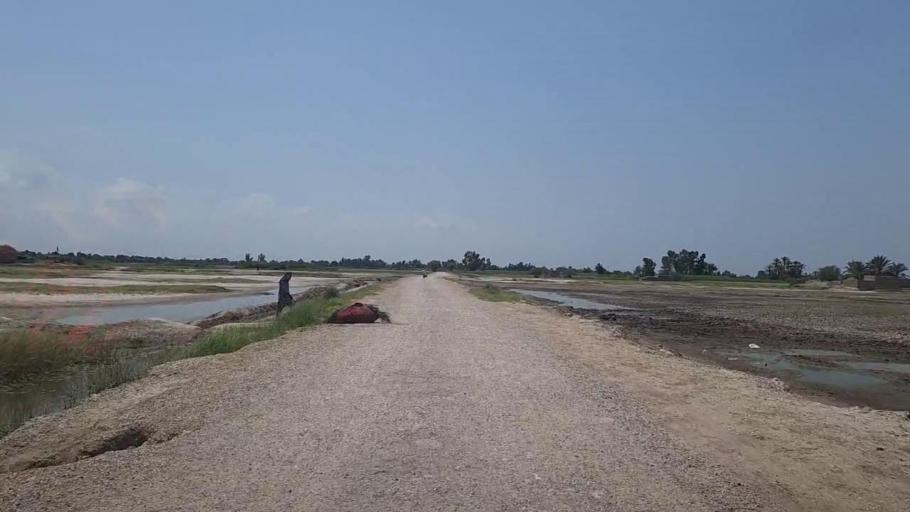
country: PK
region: Sindh
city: Ubauro
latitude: 28.1599
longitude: 69.7645
